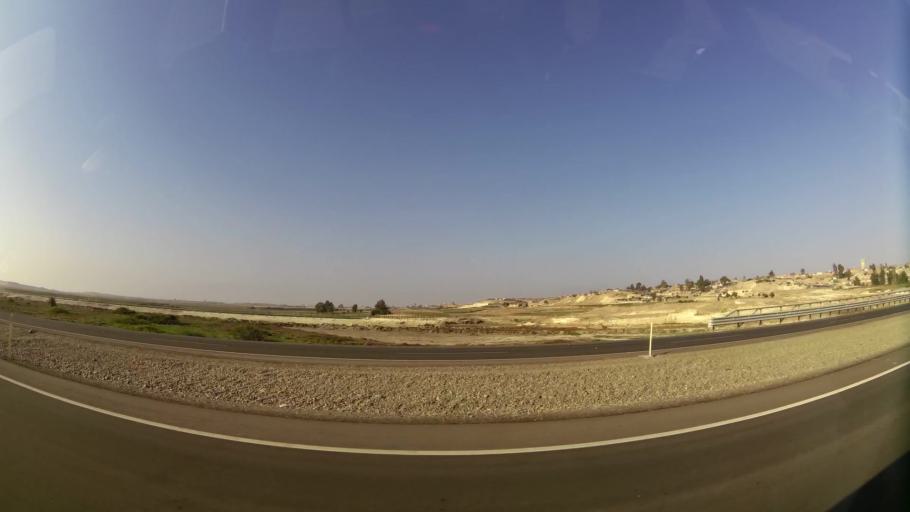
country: PE
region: Ica
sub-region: Provincia de Pisco
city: San Clemente
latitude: -13.6729
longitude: -76.1665
